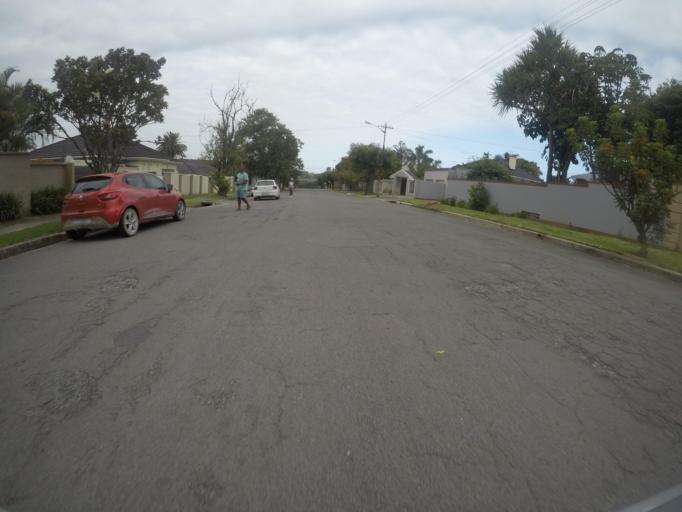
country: ZA
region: Eastern Cape
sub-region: Buffalo City Metropolitan Municipality
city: East London
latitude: -32.9903
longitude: 27.8960
